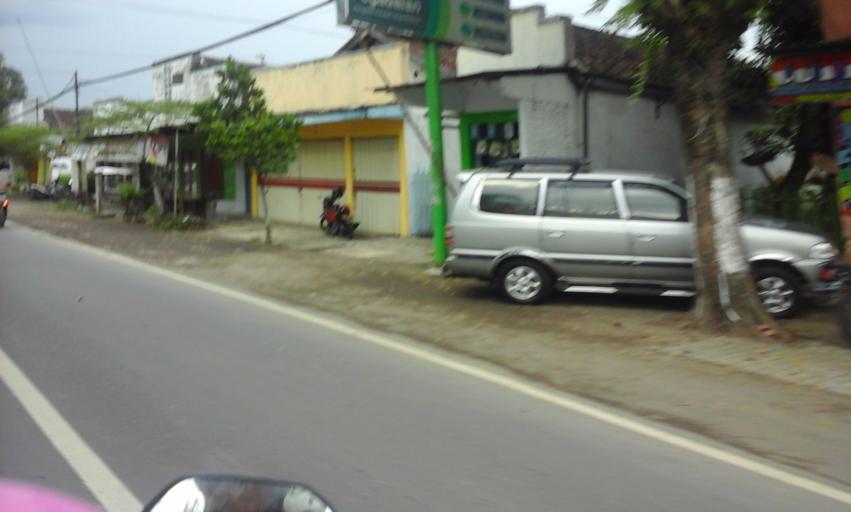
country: ID
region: East Java
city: Jenggawah
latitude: -8.2633
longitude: 113.6494
